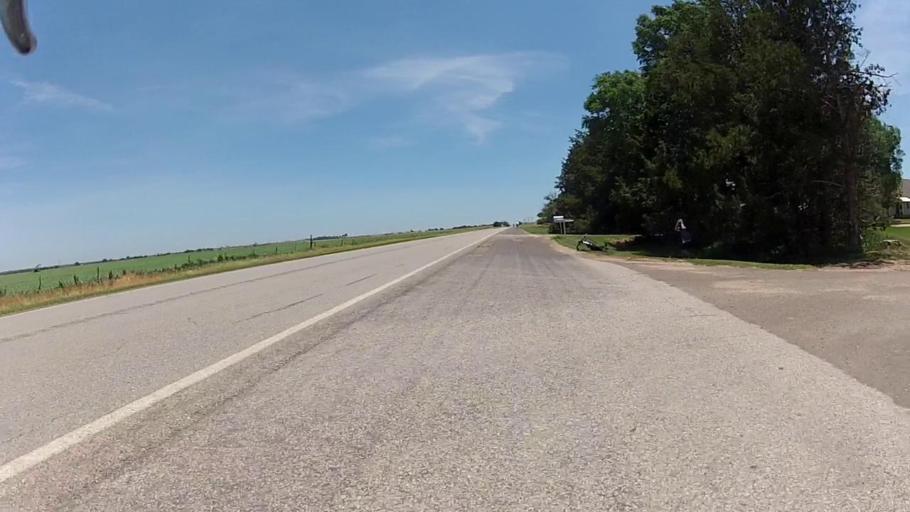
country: US
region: Kansas
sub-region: Barber County
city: Medicine Lodge
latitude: 37.2539
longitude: -98.3974
